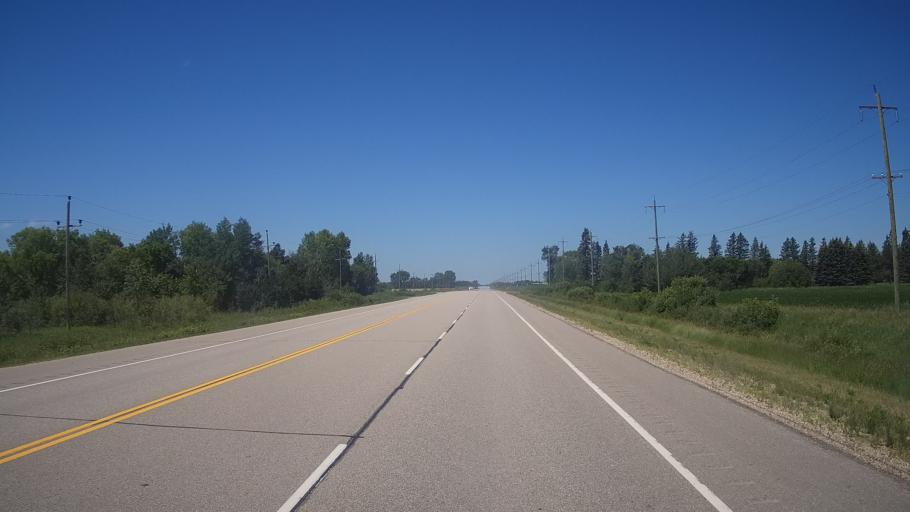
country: CA
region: Manitoba
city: Neepawa
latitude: 50.2250
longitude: -99.2802
